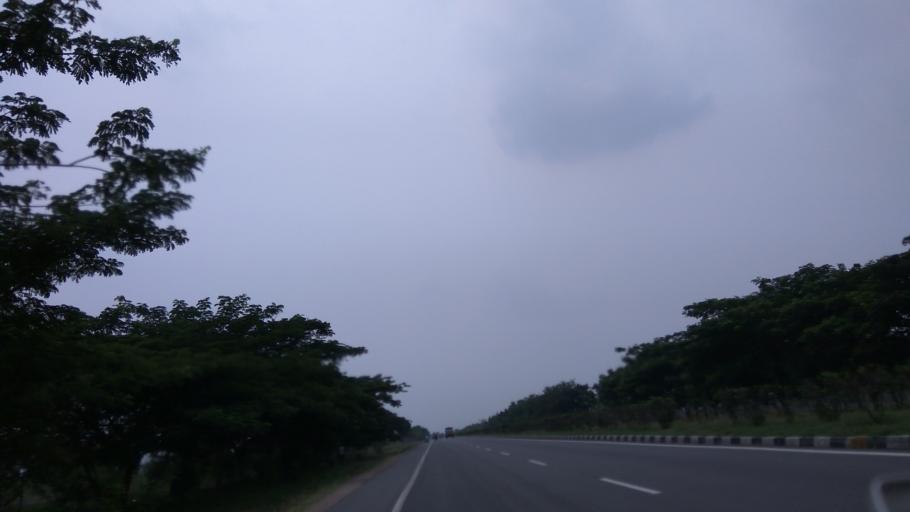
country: IN
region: Tamil Nadu
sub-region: Dharmapuri
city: Dharmapuri
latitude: 12.1249
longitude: 78.1347
